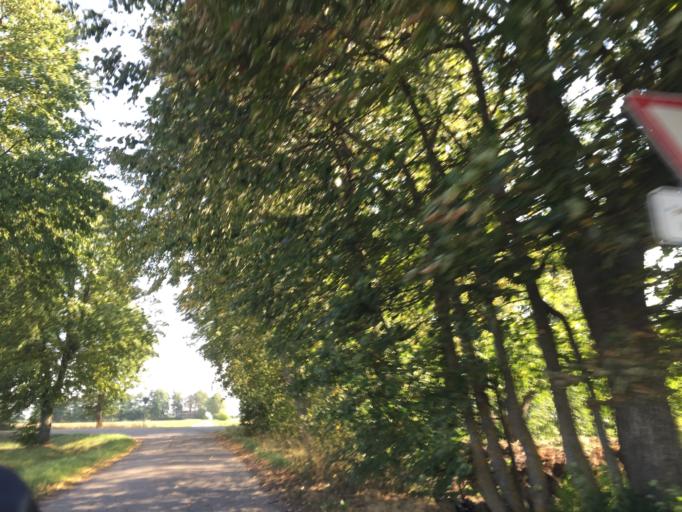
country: LV
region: Jelgava
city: Jelgava
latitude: 56.4511
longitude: 23.6803
